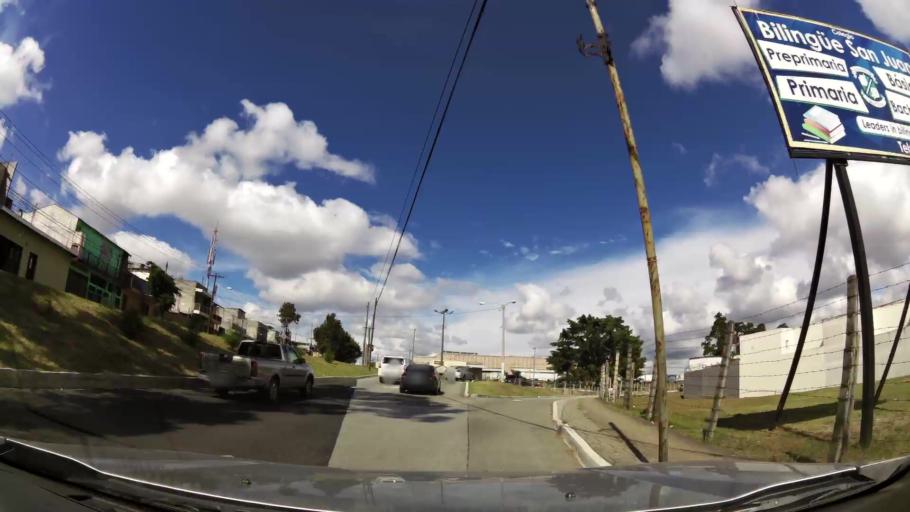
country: GT
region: Guatemala
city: Mixco
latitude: 14.6518
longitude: -90.5691
